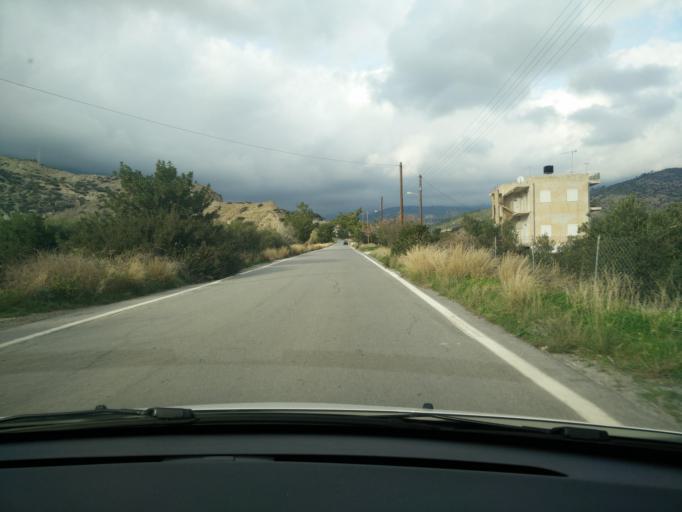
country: GR
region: Crete
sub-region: Nomos Lasithiou
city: Gra Liyia
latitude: 35.0116
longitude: 25.5836
